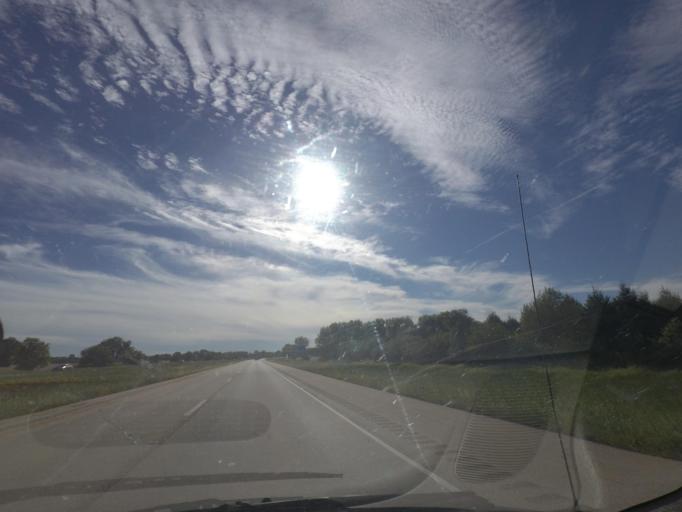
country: US
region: Illinois
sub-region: Macon County
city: Forsyth
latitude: 39.9166
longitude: -88.8645
